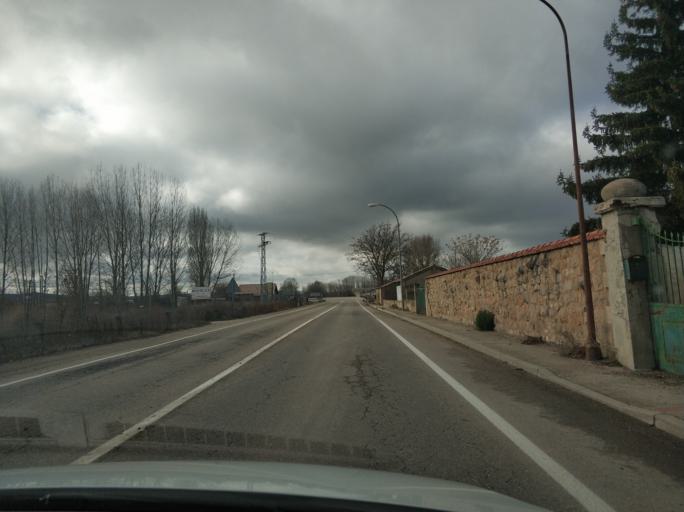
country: ES
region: Castille and Leon
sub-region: Provincia de Soria
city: San Esteban de Gormaz
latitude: 41.5712
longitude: -3.2092
